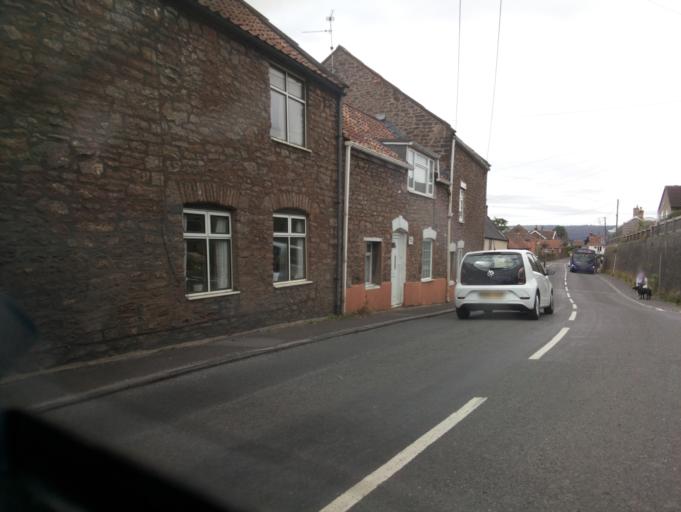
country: GB
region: England
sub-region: Somerset
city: Bradley Cross
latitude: 51.2554
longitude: -2.7501
